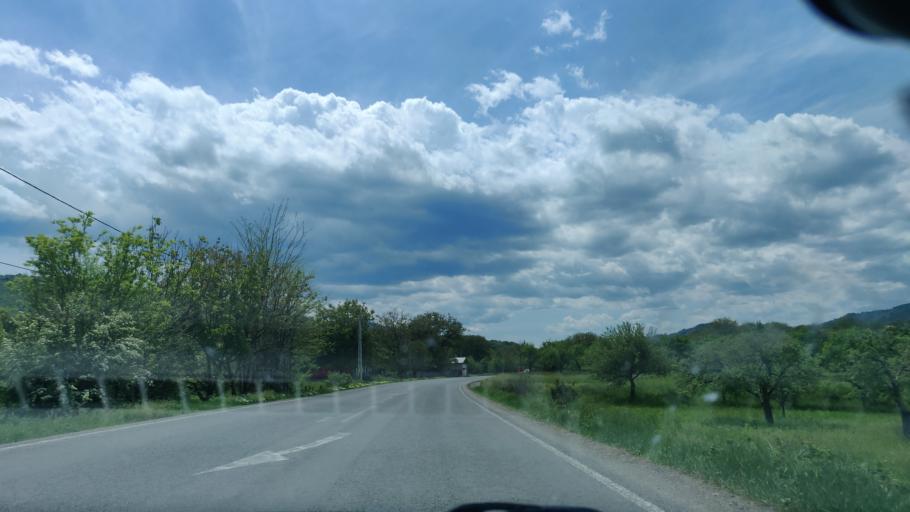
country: RO
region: Vrancea
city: Matacina
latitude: 45.8918
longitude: 26.8485
